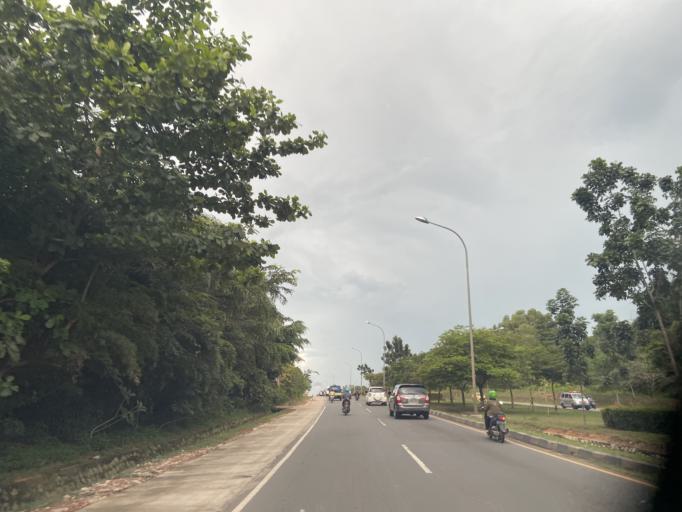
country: SG
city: Singapore
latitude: 1.0990
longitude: 104.0650
